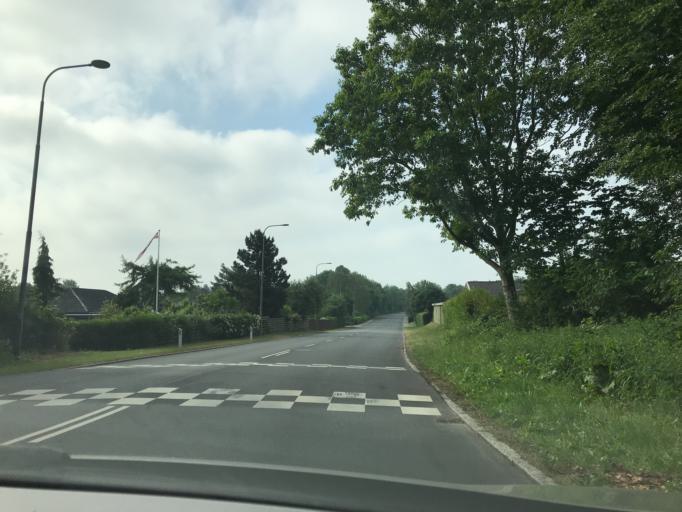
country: DK
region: South Denmark
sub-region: Odense Kommune
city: Bellinge
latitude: 55.3760
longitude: 10.3414
